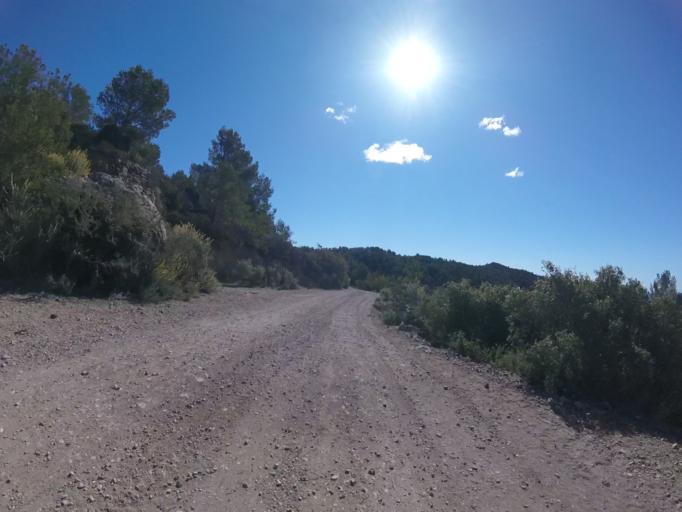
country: ES
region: Valencia
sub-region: Provincia de Castello
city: Benicassim
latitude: 40.0738
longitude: 0.0763
